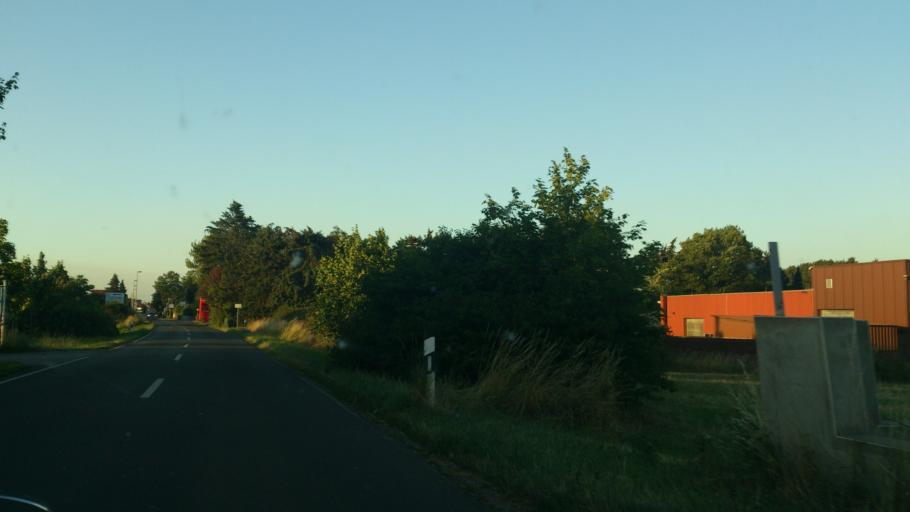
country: DE
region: Hesse
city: Raunheim
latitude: 50.0330
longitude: 8.4629
